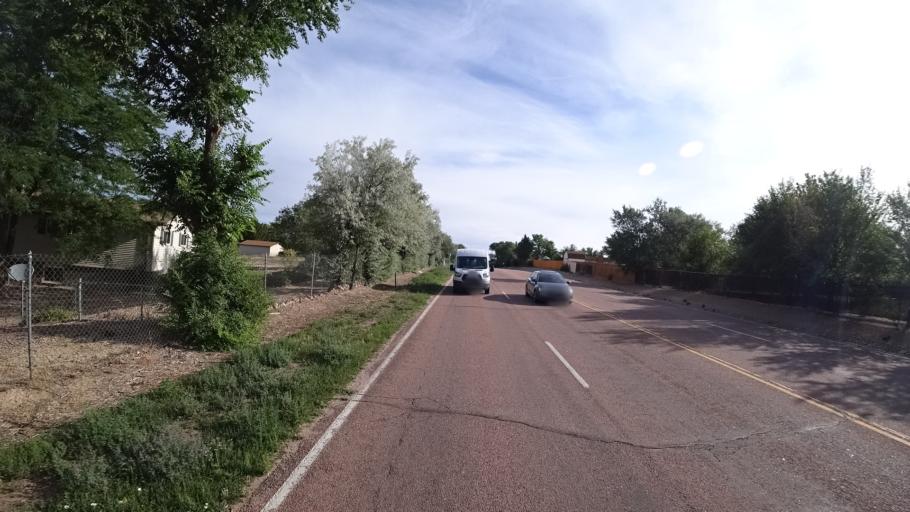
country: US
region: Colorado
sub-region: El Paso County
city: Security-Widefield
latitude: 38.7284
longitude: -104.6977
